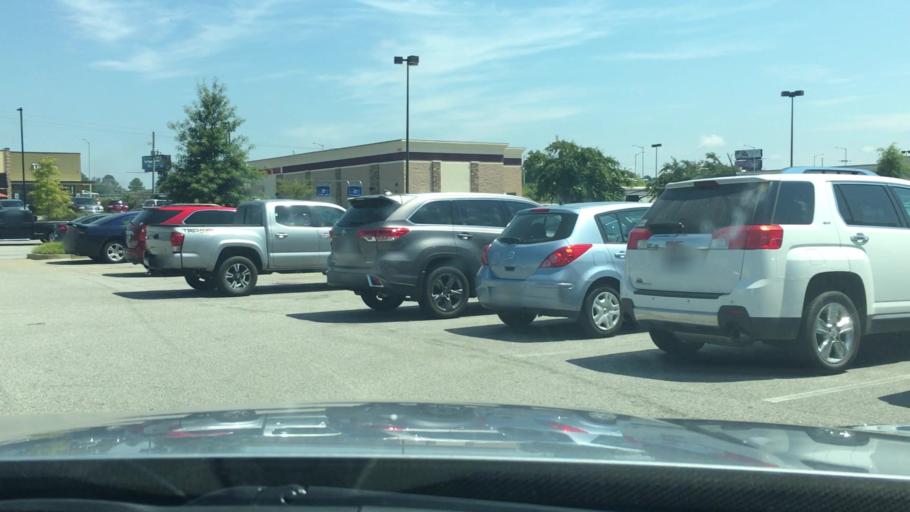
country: US
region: South Carolina
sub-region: Florence County
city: Florence
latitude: 34.1864
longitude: -79.8247
